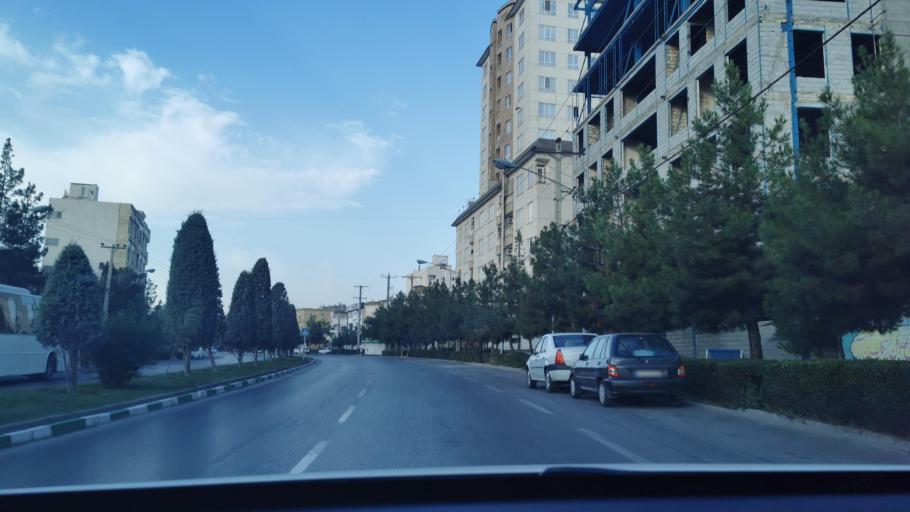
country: IR
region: Razavi Khorasan
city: Mashhad
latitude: 36.3580
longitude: 59.5030
